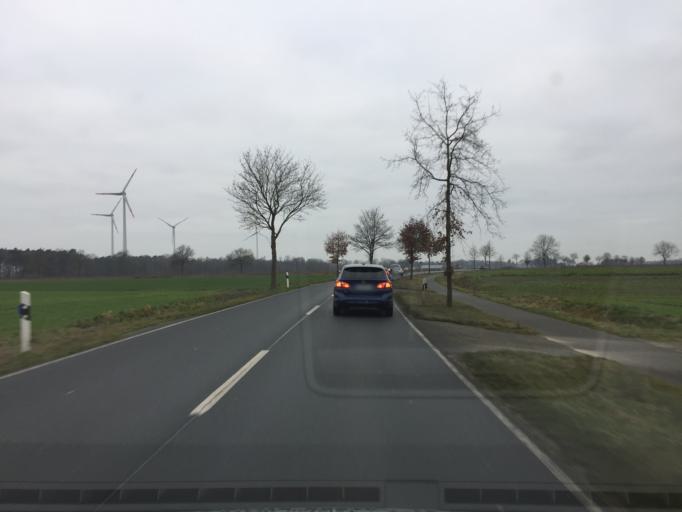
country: DE
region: Lower Saxony
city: Langwedel
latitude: 53.0071
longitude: 9.1714
